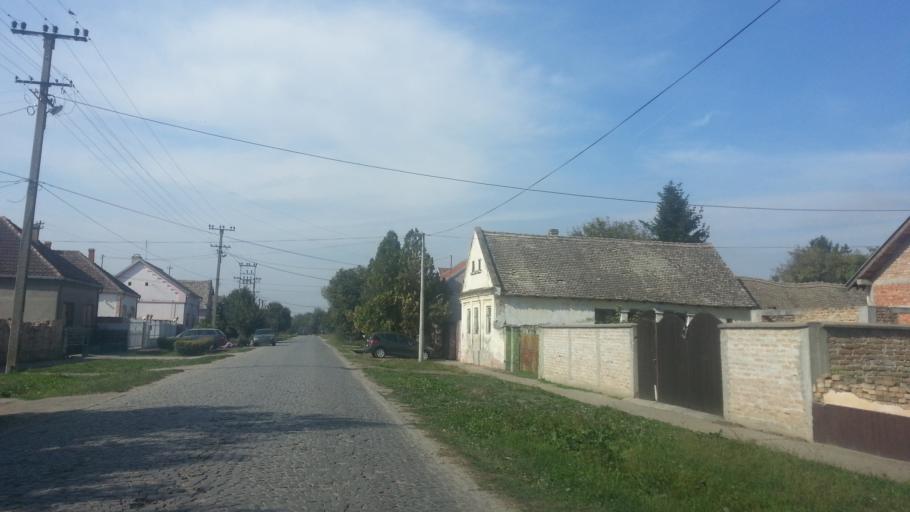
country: RS
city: Stari Banovci
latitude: 44.9954
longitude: 20.2826
